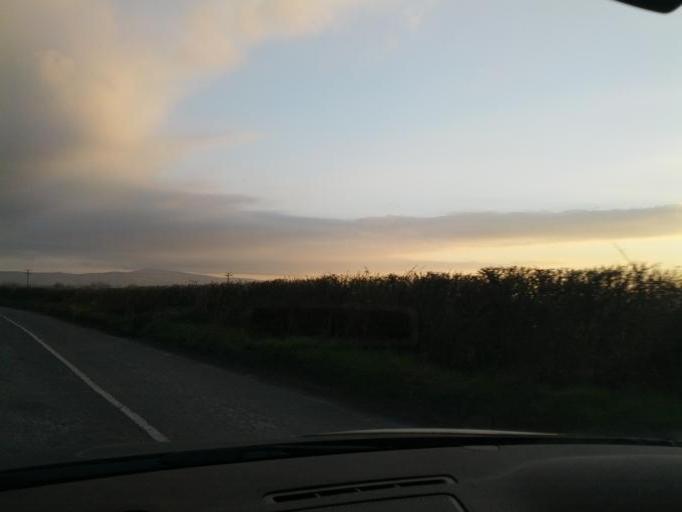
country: IE
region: Munster
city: Nenagh Bridge
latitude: 52.9040
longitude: -8.2111
